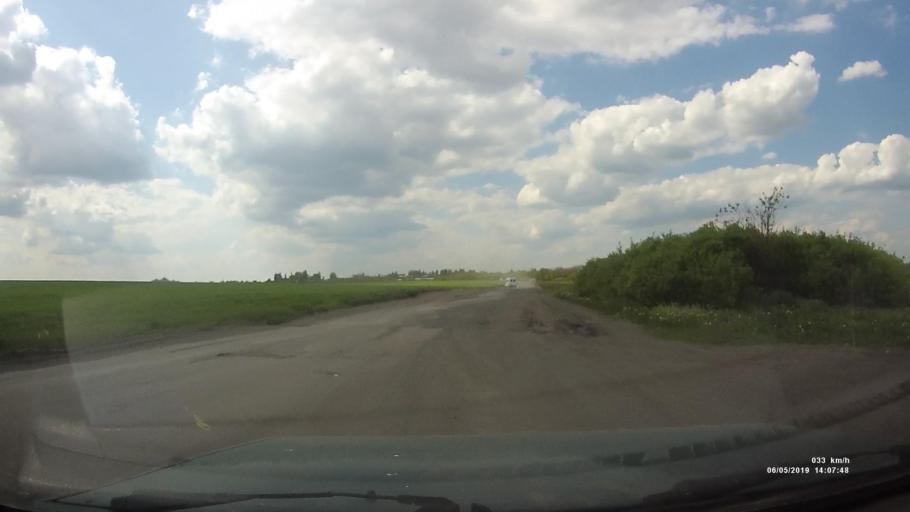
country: RU
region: Rostov
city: Shakhty
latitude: 47.6812
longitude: 40.3017
